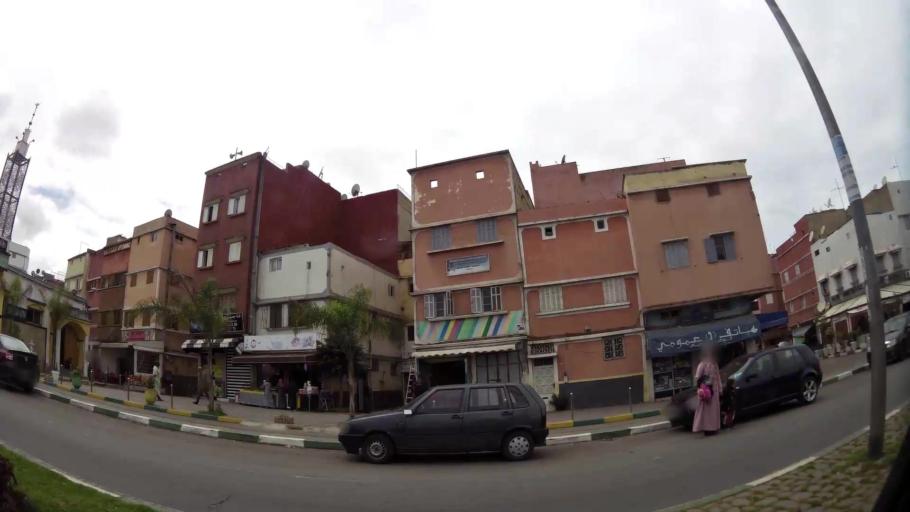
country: MA
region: Grand Casablanca
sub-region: Mediouna
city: Tit Mellil
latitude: 33.6107
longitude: -7.5015
